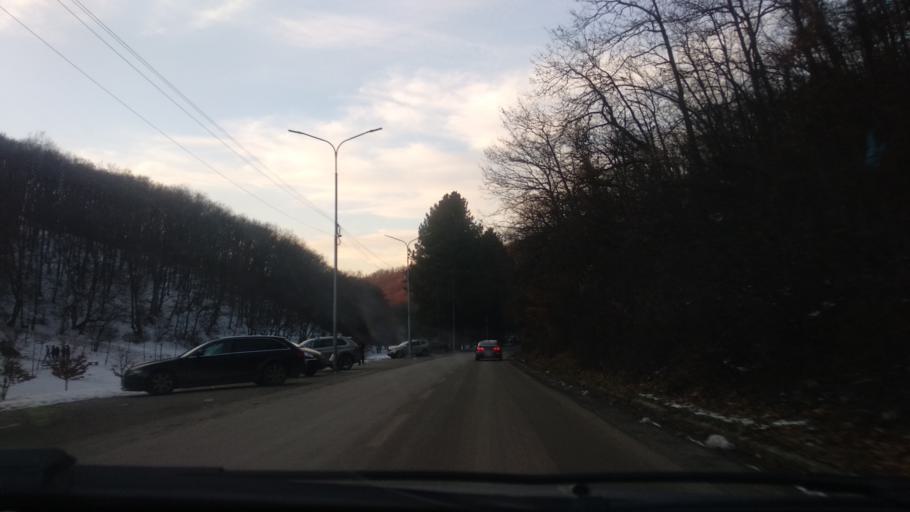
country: XK
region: Pristina
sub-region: Komuna e Prishtines
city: Pristina
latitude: 42.6727
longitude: 21.2158
